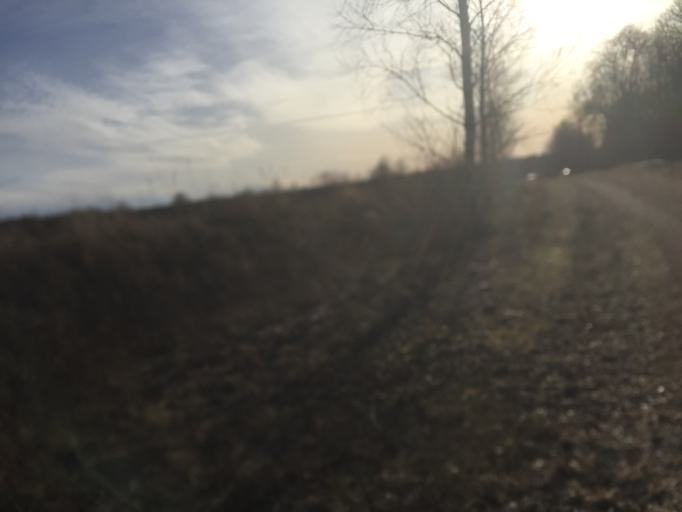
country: SE
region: Joenkoeping
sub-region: Aneby Kommun
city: Aneby
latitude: 57.8262
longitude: 14.8183
